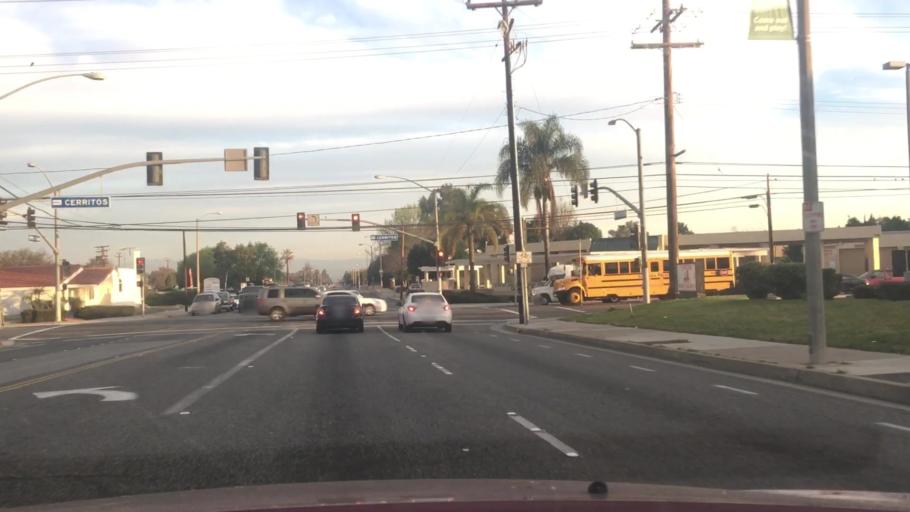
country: US
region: California
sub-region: Orange County
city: Stanton
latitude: 33.8096
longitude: -118.0020
